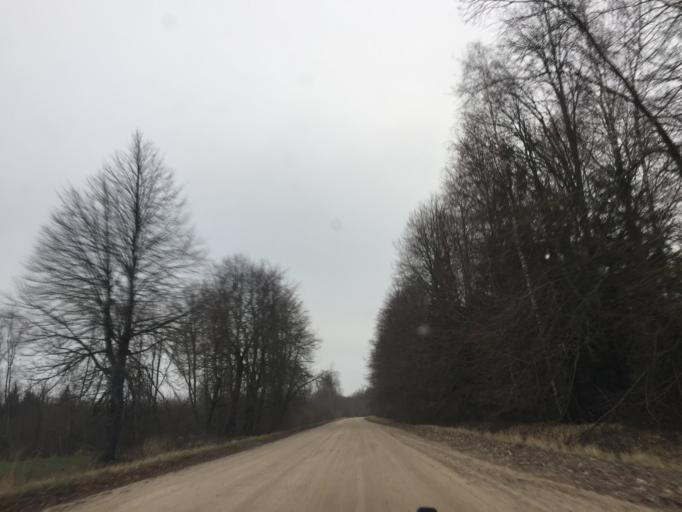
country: LV
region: Limbazu Rajons
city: Limbazi
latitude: 57.5857
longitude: 24.5137
